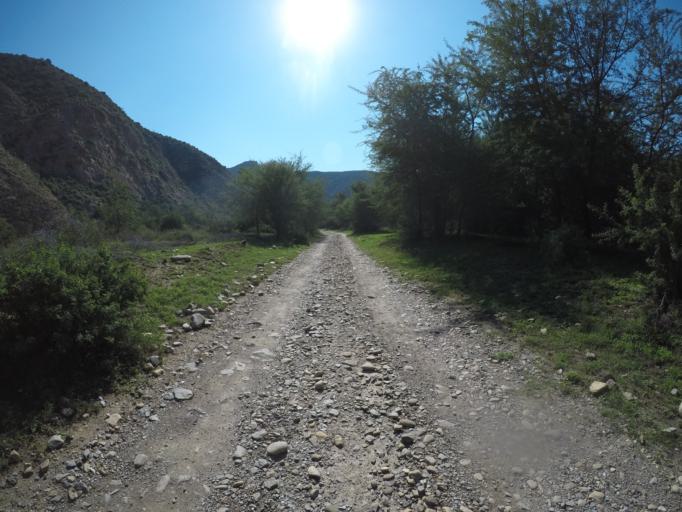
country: ZA
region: Eastern Cape
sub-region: Cacadu District Municipality
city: Kareedouw
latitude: -33.6594
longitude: 24.3666
